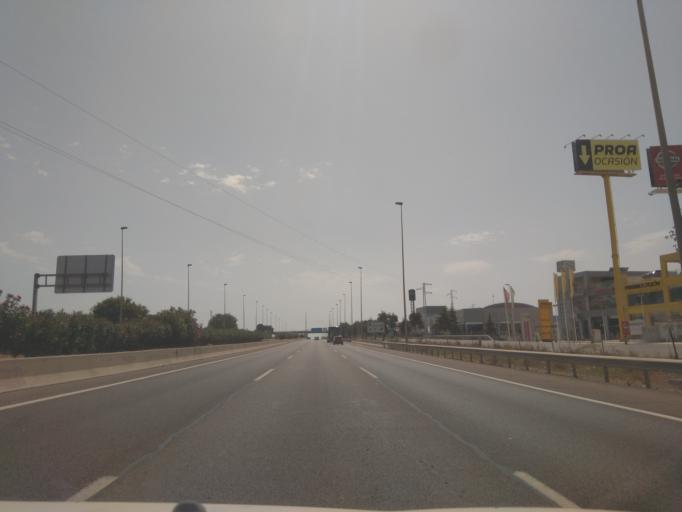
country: ES
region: Valencia
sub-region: Provincia de Valencia
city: Alfafar
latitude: 39.4046
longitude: -0.3843
